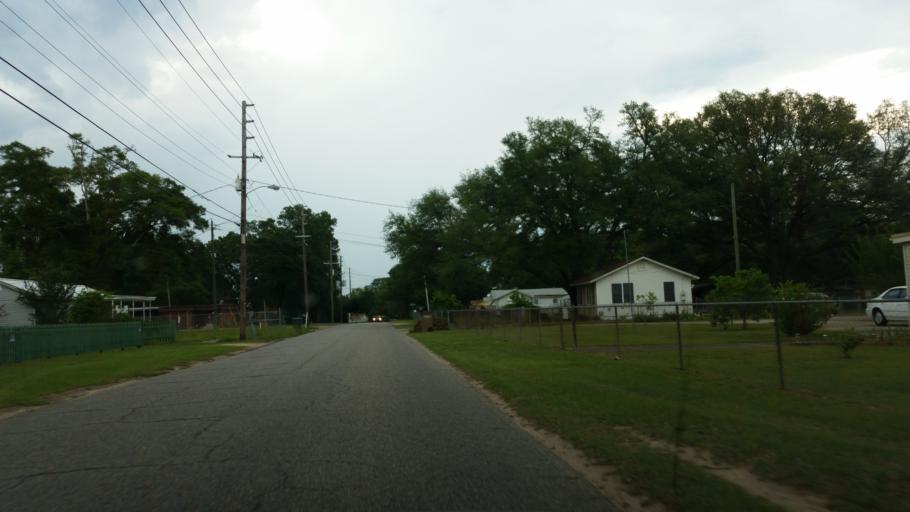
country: US
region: Florida
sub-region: Escambia County
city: Brent
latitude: 30.4681
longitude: -87.2207
